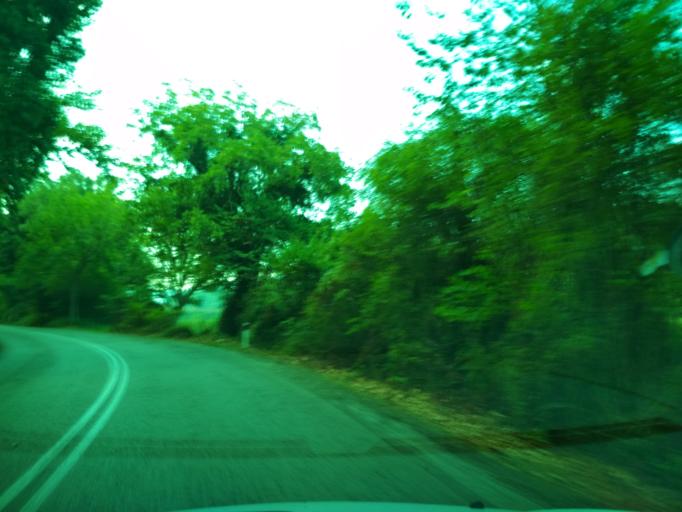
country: GR
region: Central Greece
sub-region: Nomos Evvoias
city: Prokopion
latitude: 38.7611
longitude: 23.4790
